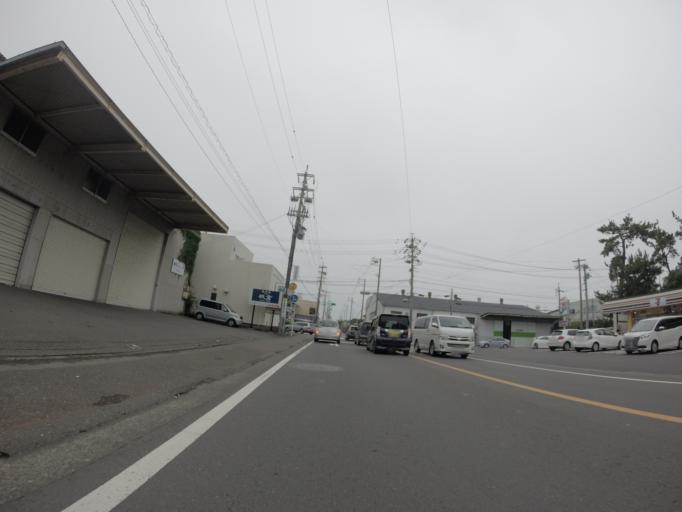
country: JP
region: Shizuoka
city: Shizuoka-shi
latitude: 34.9486
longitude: 138.3981
